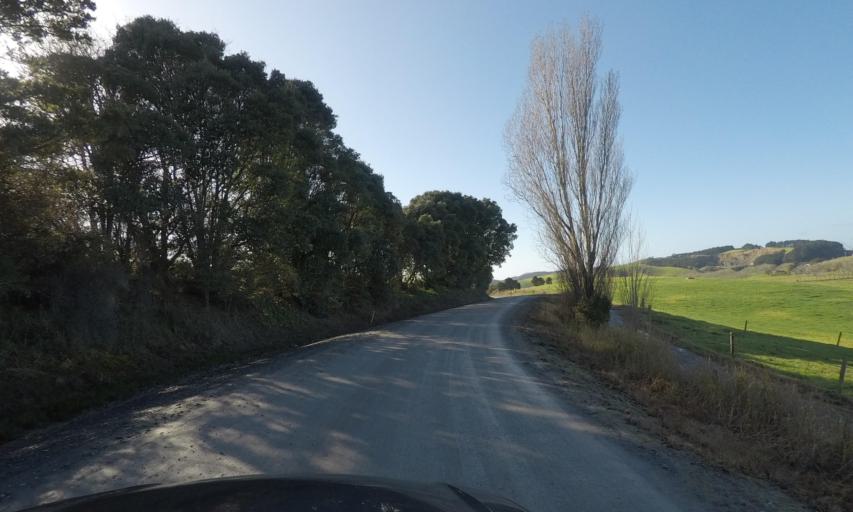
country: NZ
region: Auckland
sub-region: Auckland
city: Wellsford
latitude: -36.1614
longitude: 174.6056
